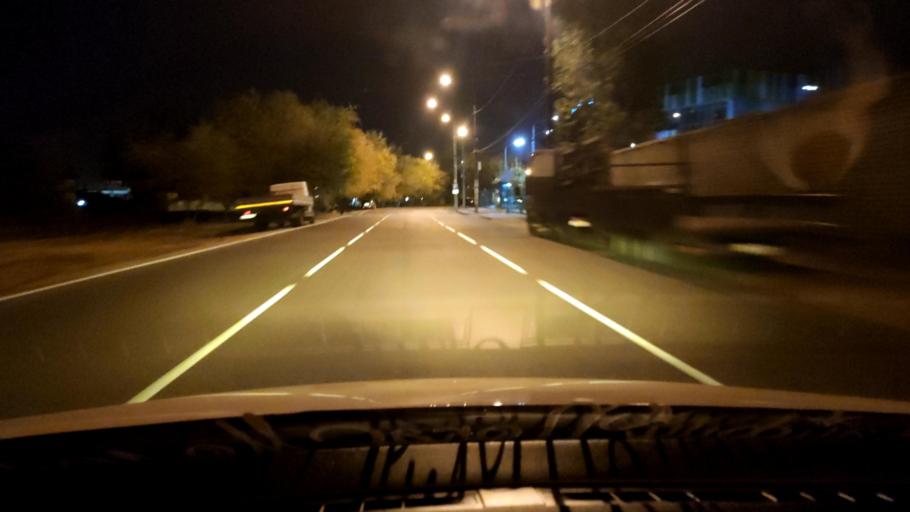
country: RU
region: Voronezj
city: Voronezh
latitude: 51.6781
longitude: 39.1675
